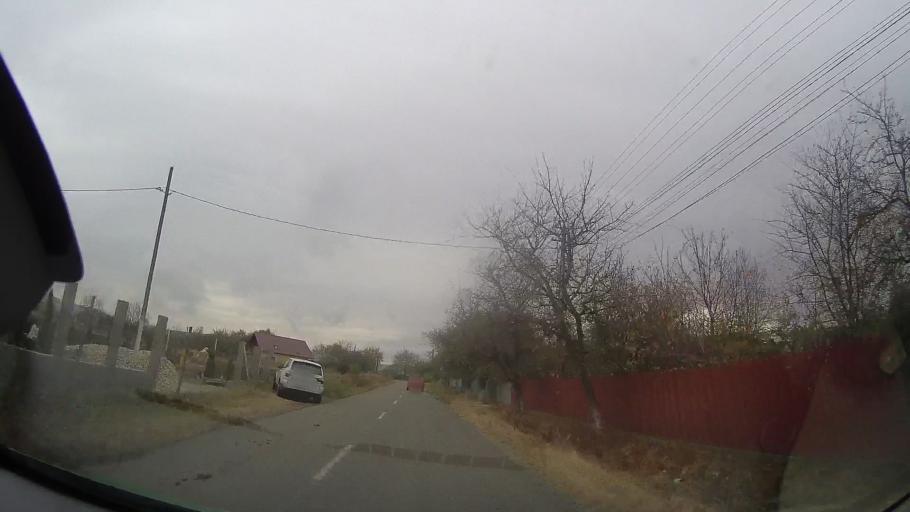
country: RO
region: Prahova
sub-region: Comuna Fantanele
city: Fantanele
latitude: 45.0146
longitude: 26.3798
